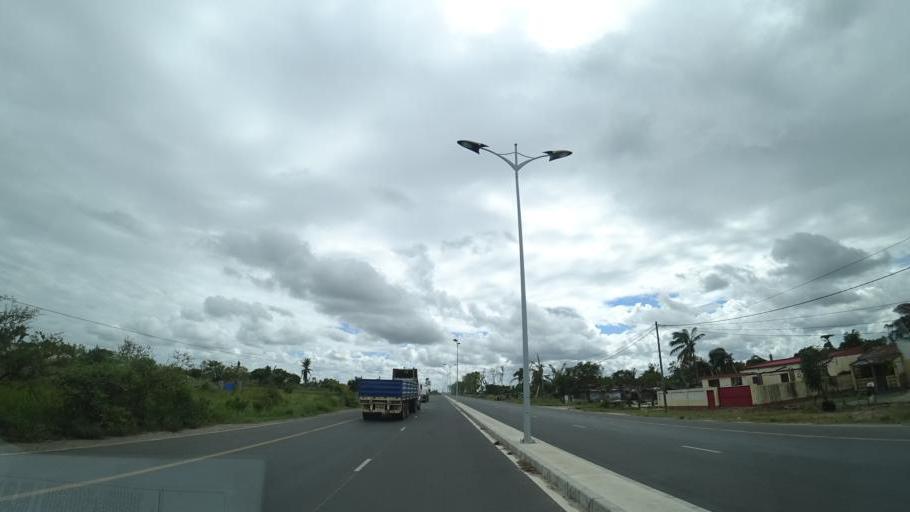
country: MZ
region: Sofala
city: Dondo
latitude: -19.6896
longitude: 34.7778
